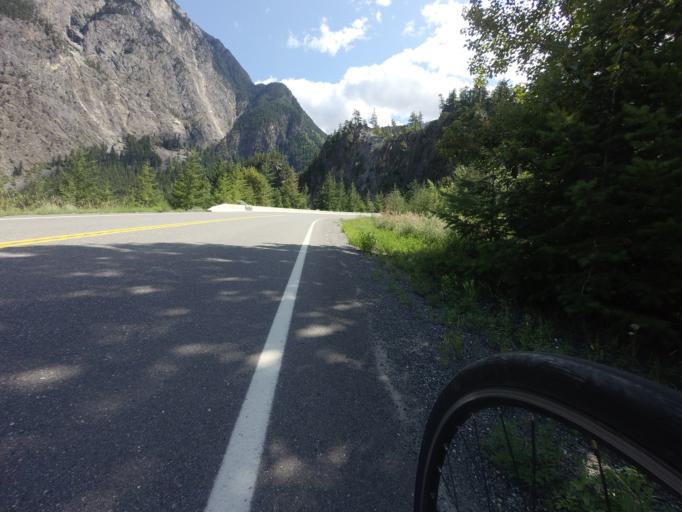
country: CA
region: British Columbia
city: Lillooet
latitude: 50.6617
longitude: -121.9869
